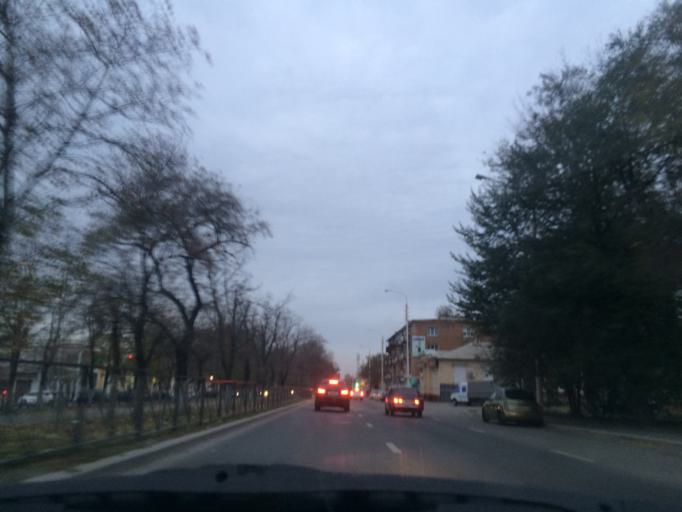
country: RU
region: Rostov
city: Novocherkassk
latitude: 47.4218
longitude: 40.0786
